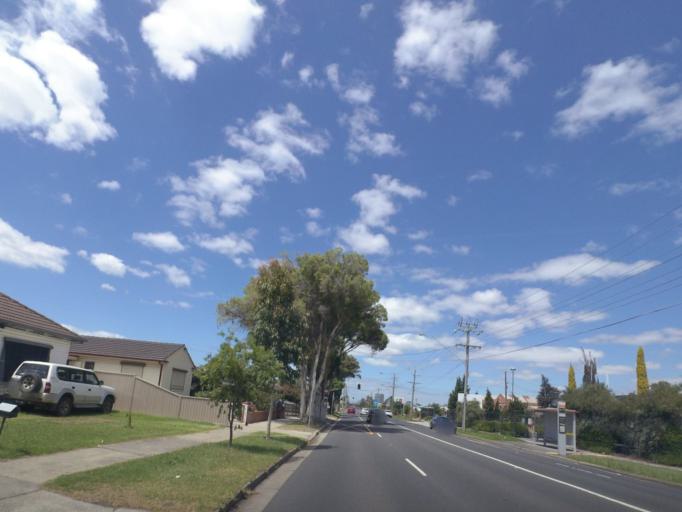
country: AU
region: Victoria
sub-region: Brimbank
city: Sunshine North
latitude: -37.7707
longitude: 144.8300
